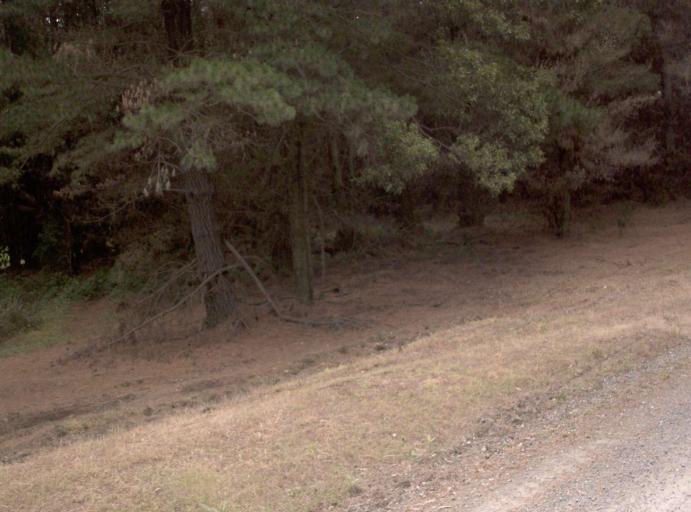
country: AU
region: Victoria
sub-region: Latrobe
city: Traralgon
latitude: -38.3854
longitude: 146.6635
